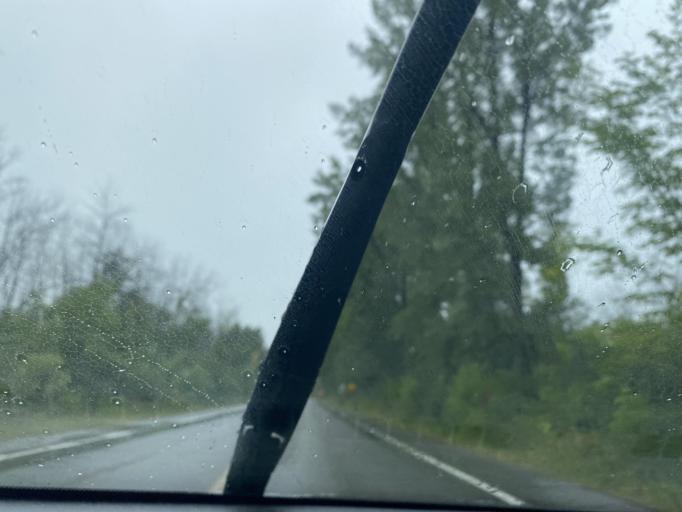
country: CA
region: Quebec
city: Baie-D'Urfe
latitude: 45.4468
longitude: -73.9202
